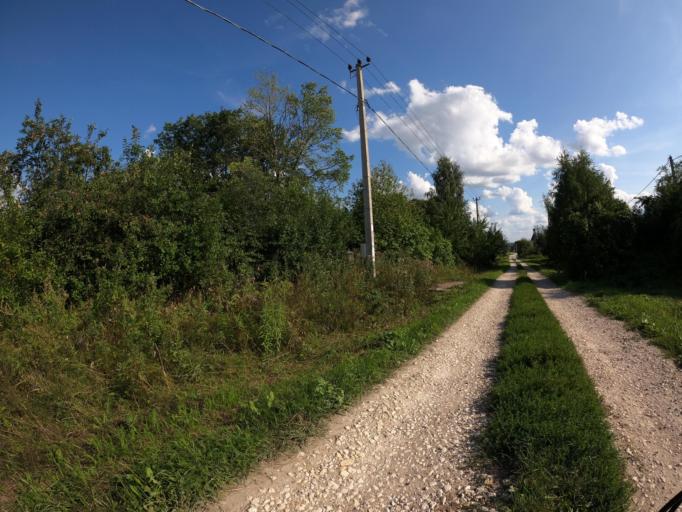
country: RU
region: Moskovskaya
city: Troitskoye
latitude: 55.2157
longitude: 38.4877
